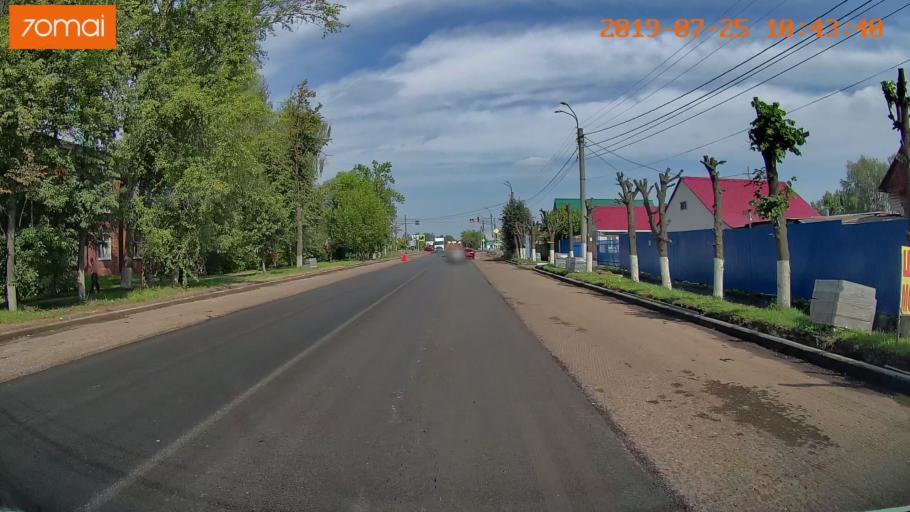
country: RU
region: Ivanovo
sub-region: Gorod Ivanovo
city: Ivanovo
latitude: 57.0376
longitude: 40.9688
